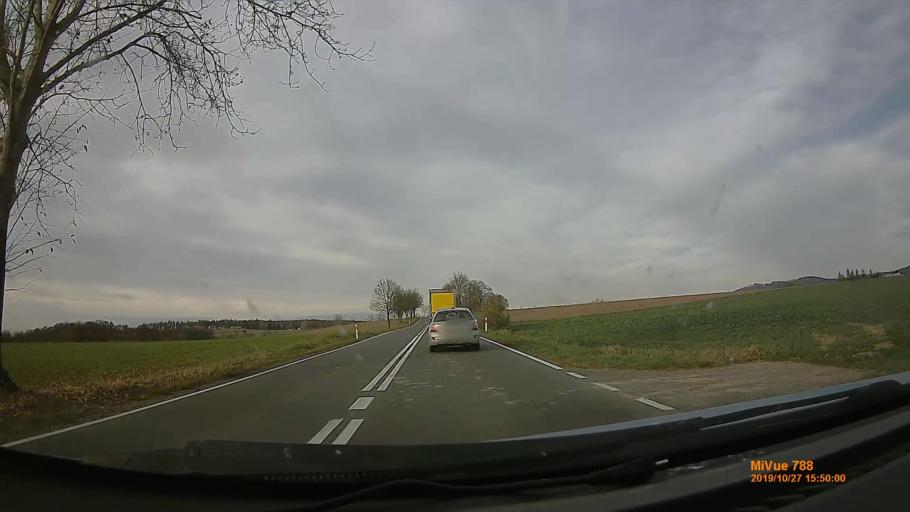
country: PL
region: Lower Silesian Voivodeship
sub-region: Powiat klodzki
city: Bozkow
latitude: 50.5134
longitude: 16.5847
